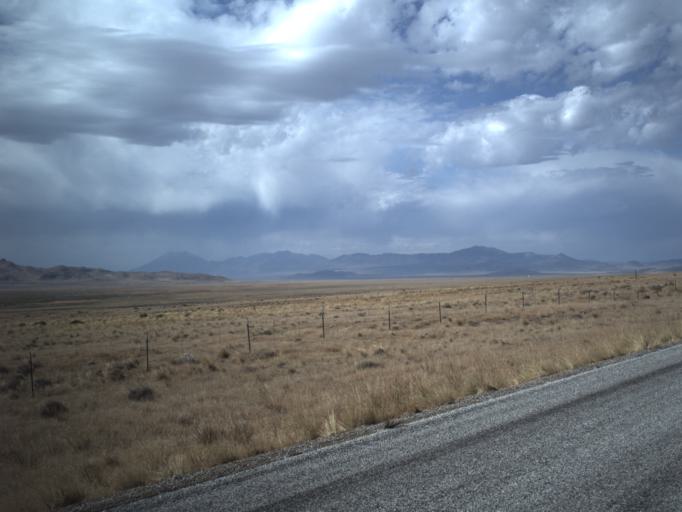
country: US
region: Utah
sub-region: Tooele County
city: Wendover
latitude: 41.4414
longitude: -113.6993
